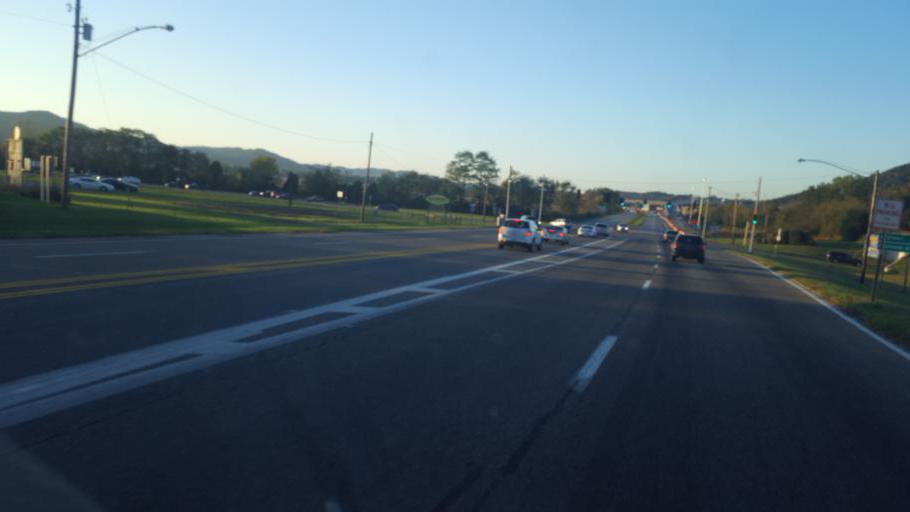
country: US
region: Ohio
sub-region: Scioto County
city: Lucasville
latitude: 38.8844
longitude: -82.9965
